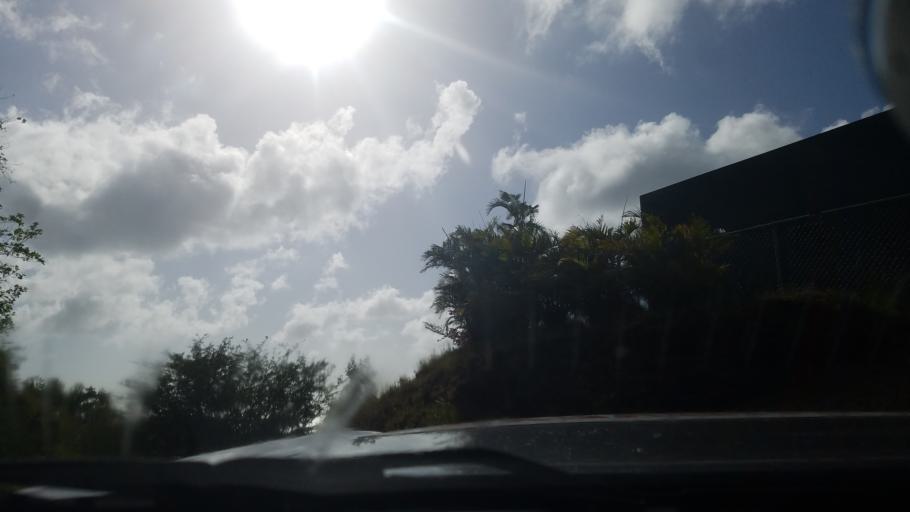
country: LC
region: Gros-Islet
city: Gros Islet
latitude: 14.0609
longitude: -60.9702
